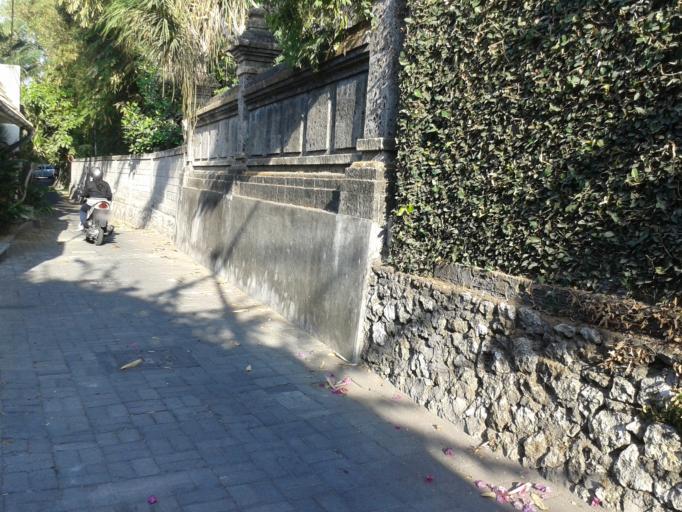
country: ID
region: Bali
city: Kuta
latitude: -8.7038
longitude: 115.1720
